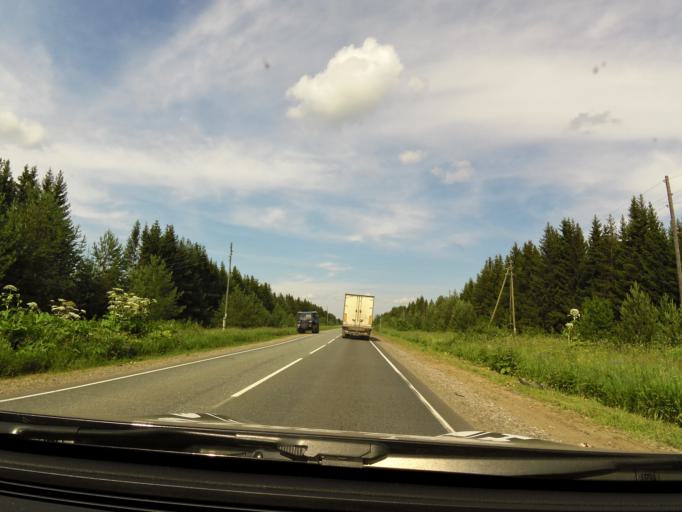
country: RU
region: Kirov
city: Slobodskoy
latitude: 58.7355
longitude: 50.2896
